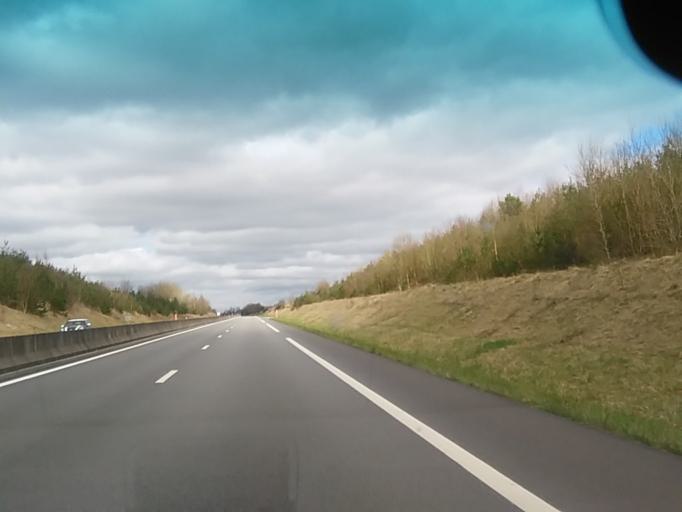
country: FR
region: Haute-Normandie
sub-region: Departement de l'Eure
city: Bourg-Achard
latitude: 49.3377
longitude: 0.8326
